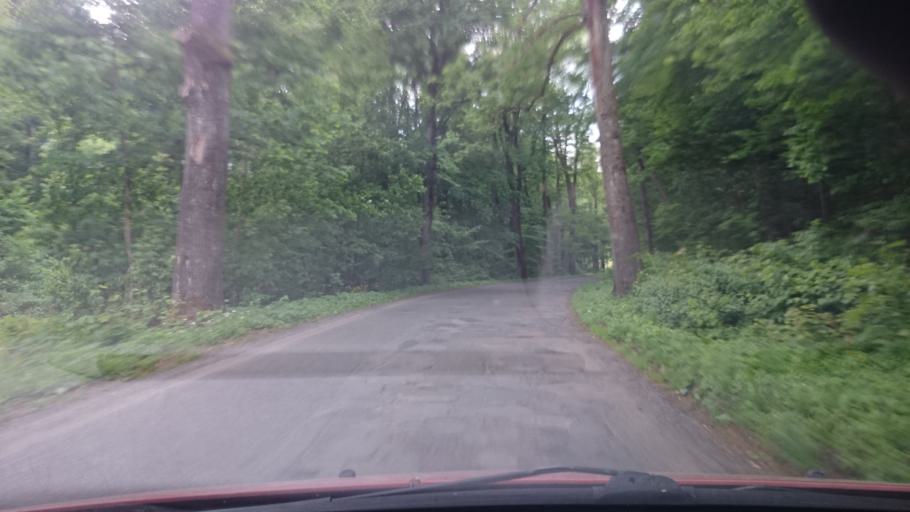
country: PL
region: Lower Silesian Voivodeship
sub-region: Powiat klodzki
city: Bystrzyca Klodzka
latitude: 50.3014
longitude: 16.5718
